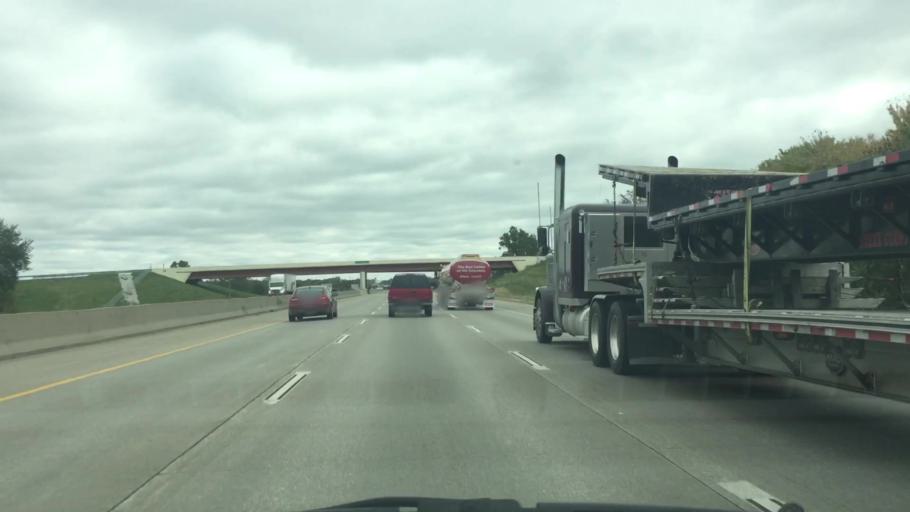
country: US
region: Iowa
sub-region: Polk County
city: Saylorville
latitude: 41.6501
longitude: -93.6553
